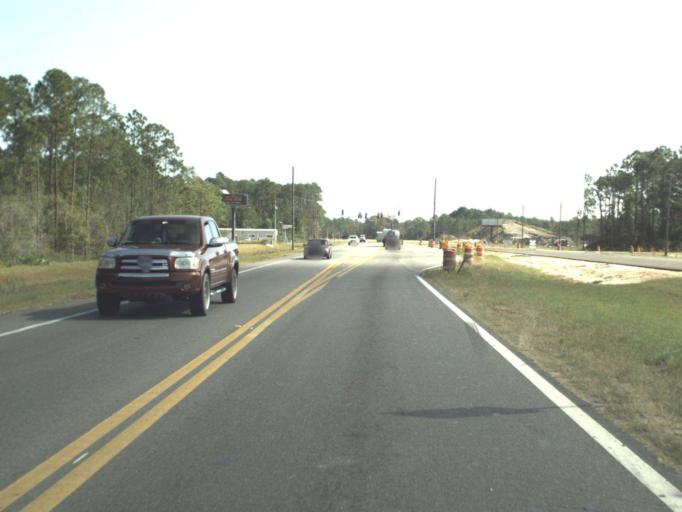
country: US
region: Florida
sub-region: Walton County
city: Freeport
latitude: 30.4437
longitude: -86.1404
